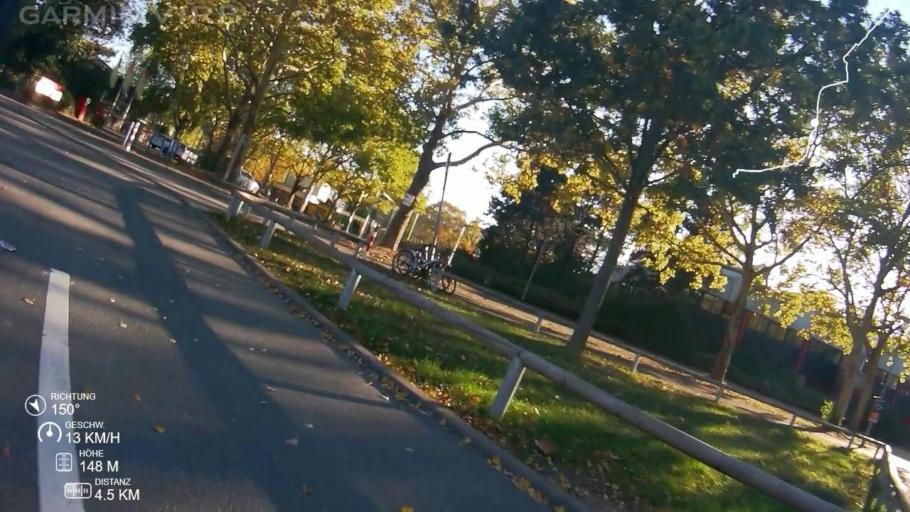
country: DE
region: Hesse
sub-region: Regierungsbezirk Darmstadt
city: Darmstadt
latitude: 49.8916
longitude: 8.6626
